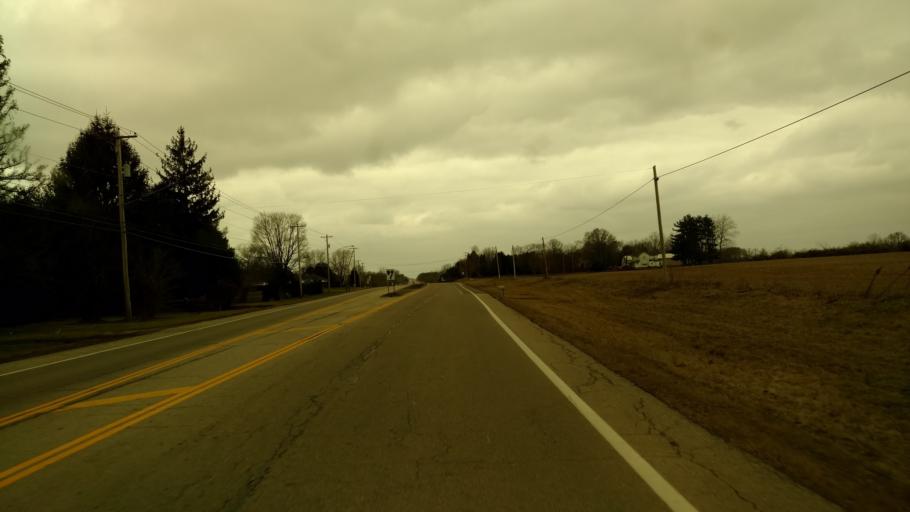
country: US
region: Ohio
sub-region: Licking County
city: Etna
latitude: 39.9590
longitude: -82.6063
